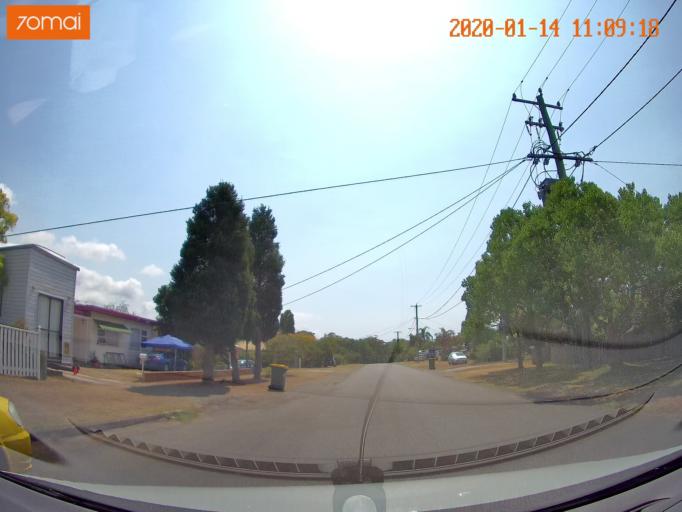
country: AU
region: New South Wales
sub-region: Lake Macquarie Shire
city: Dora Creek
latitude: -33.0963
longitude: 151.4760
